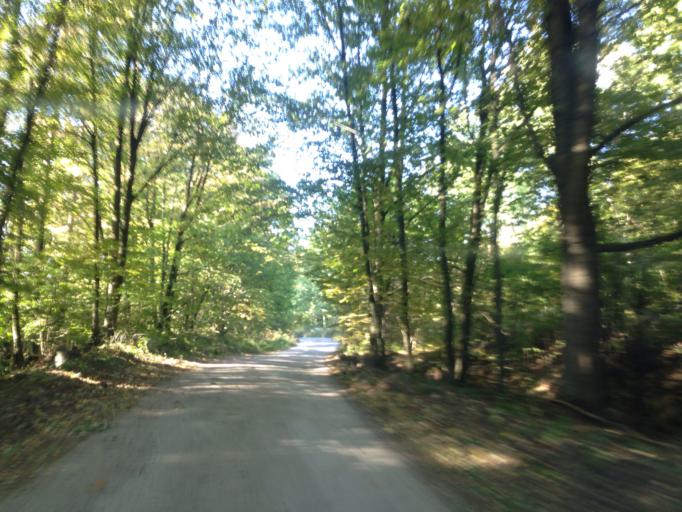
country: PL
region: Kujawsko-Pomorskie
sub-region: Powiat brodnicki
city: Gorzno
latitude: 53.2376
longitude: 19.6906
